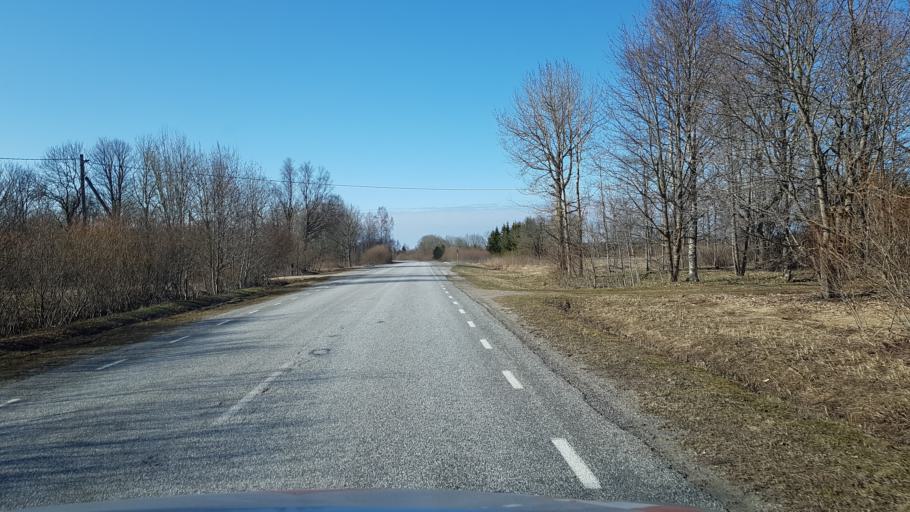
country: EE
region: Laeaene-Virumaa
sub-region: Haljala vald
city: Haljala
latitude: 59.4923
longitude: 26.1442
